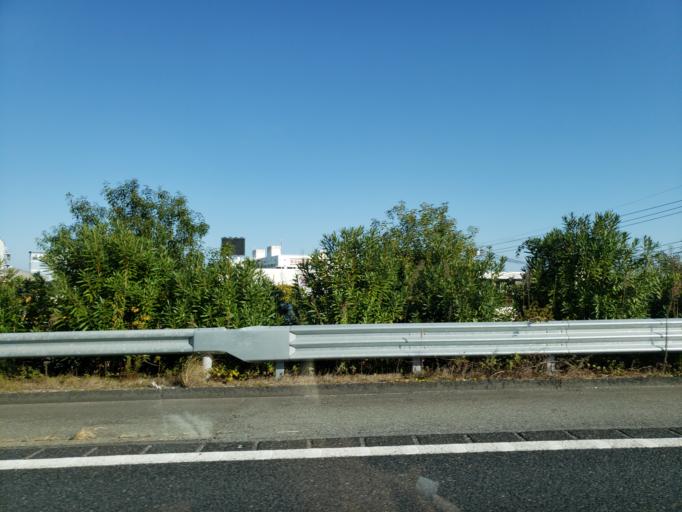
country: JP
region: Hyogo
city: Akashi
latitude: 34.7157
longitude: 134.9288
